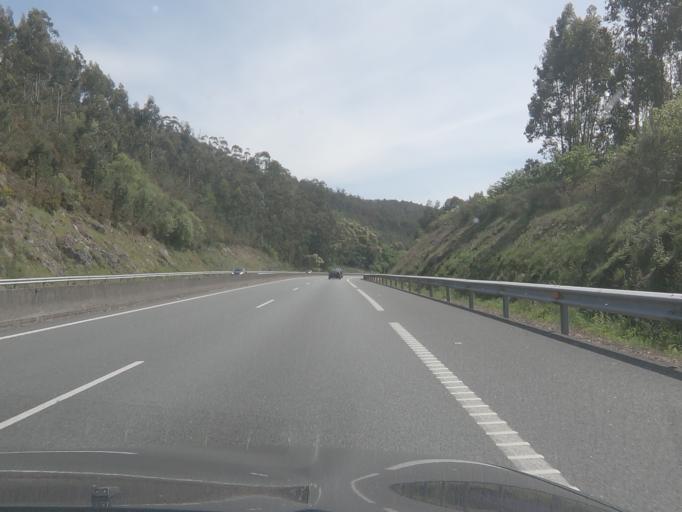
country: ES
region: Galicia
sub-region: Provincia da Coruna
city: Padron
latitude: 42.7680
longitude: -8.6446
